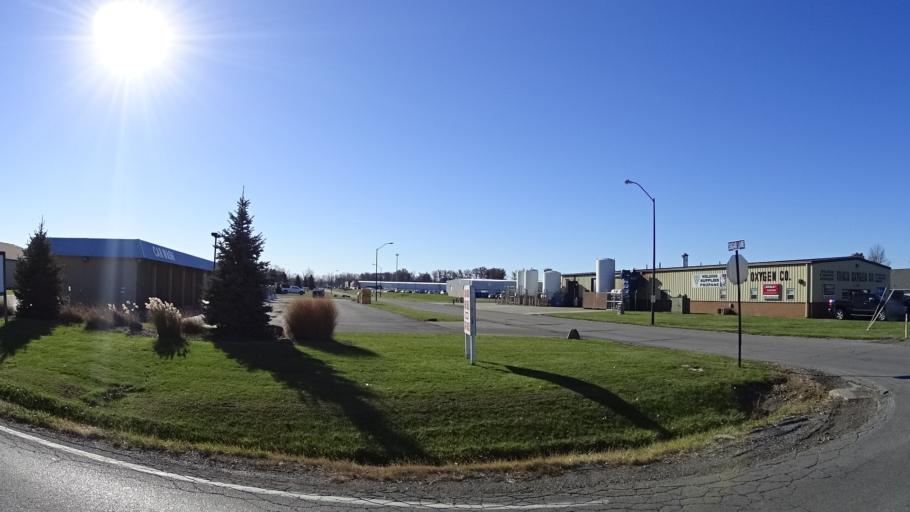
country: US
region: Ohio
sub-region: Lorain County
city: Elyria
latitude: 41.3632
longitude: -82.0726
